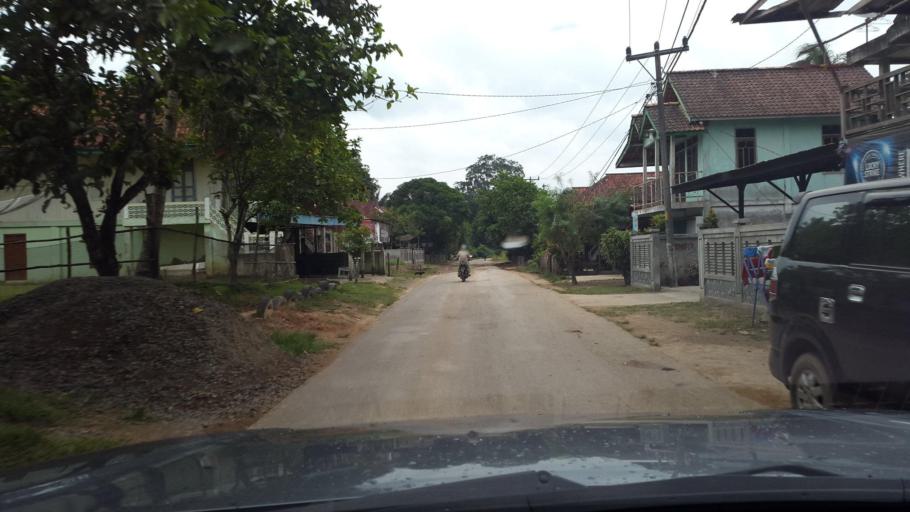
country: ID
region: South Sumatra
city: Sekayu
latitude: -3.0393
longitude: 103.7701
